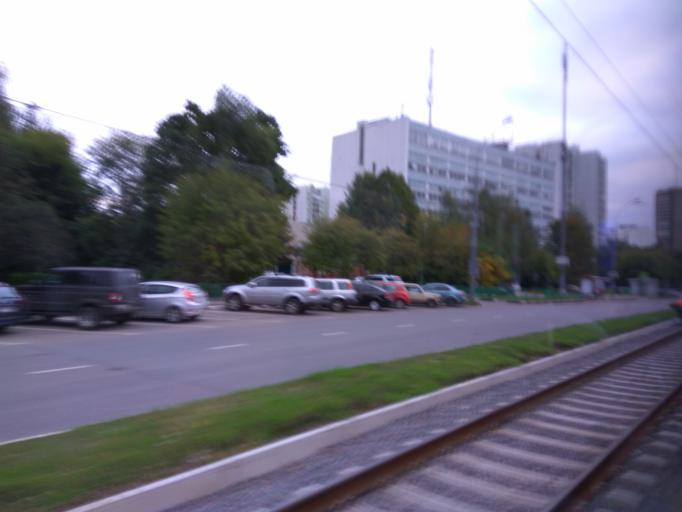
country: RU
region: Moscow
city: Chertanovo Yuzhnoye
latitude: 55.6012
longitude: 37.5890
